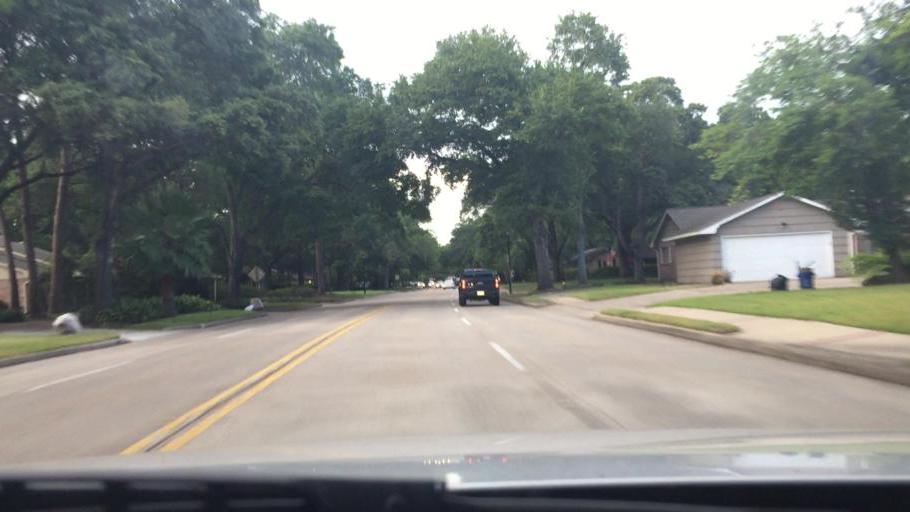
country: US
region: Texas
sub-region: Harris County
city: Hunters Creek Village
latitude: 29.7407
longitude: -95.4769
